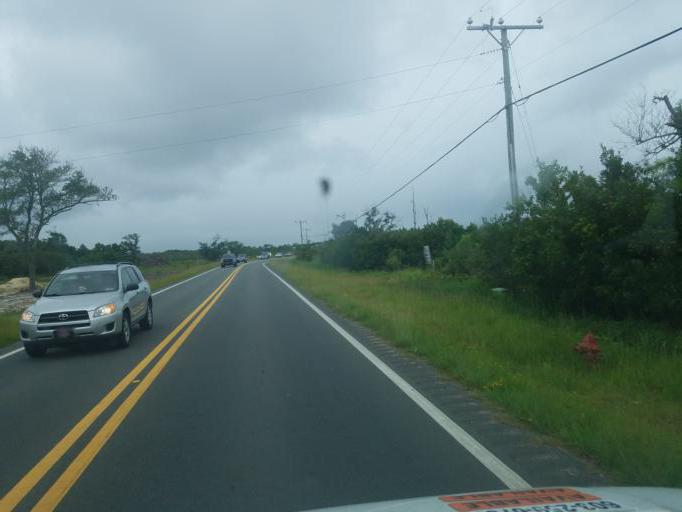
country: US
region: North Carolina
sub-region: Dare County
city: Wanchese
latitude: 35.8542
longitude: -75.6449
